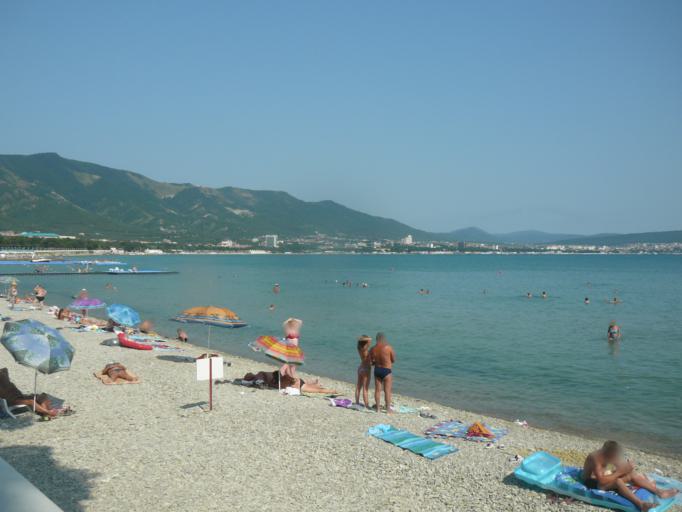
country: RU
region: Krasnodarskiy
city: Gelendzhik
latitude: 44.5844
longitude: 38.0290
